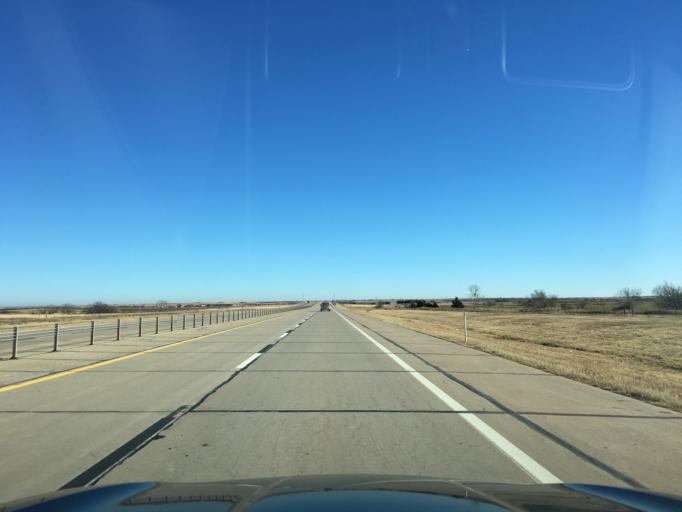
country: US
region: Oklahoma
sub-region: Noble County
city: Perry
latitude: 36.3990
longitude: -97.2898
